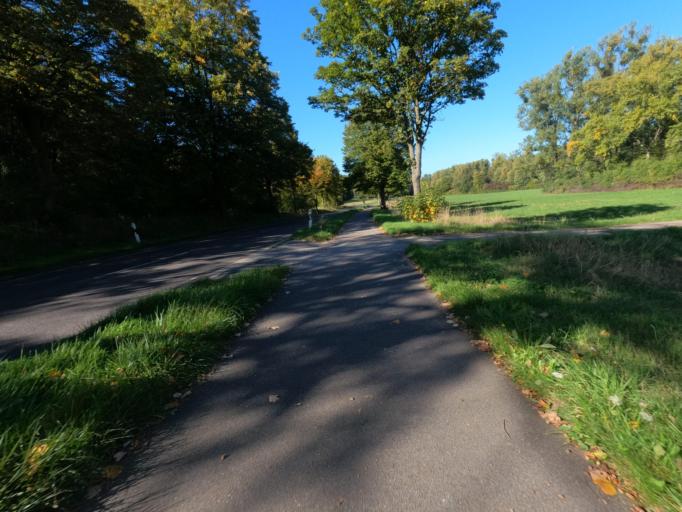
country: DE
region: North Rhine-Westphalia
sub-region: Regierungsbezirk Koln
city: Aldenhoven
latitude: 50.9330
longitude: 6.3107
